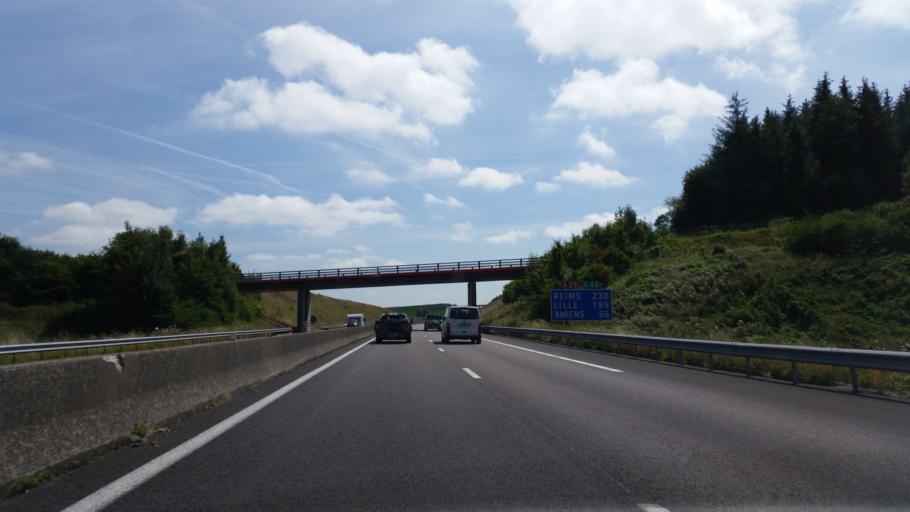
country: FR
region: Haute-Normandie
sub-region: Departement de la Seine-Maritime
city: Neufchatel-en-Bray
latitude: 49.7545
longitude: 1.4987
